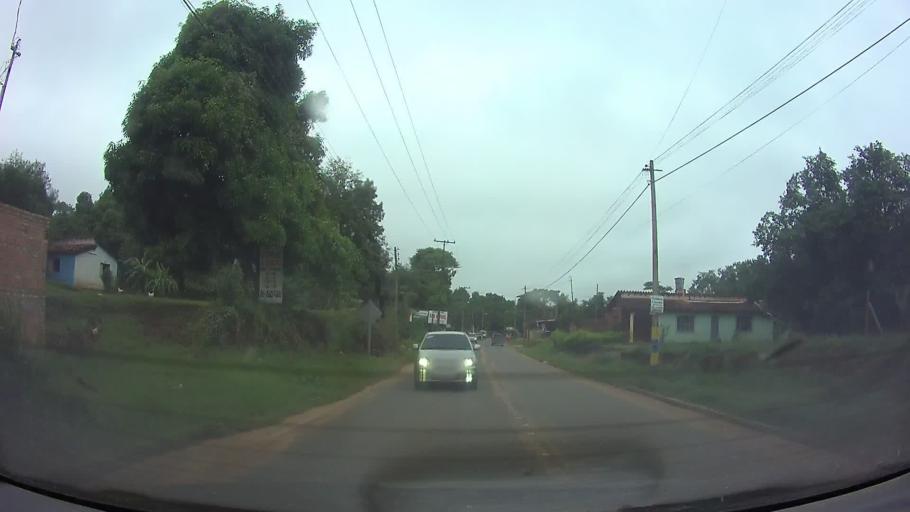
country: PY
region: Central
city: San Lorenzo
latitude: -25.3069
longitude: -57.4907
